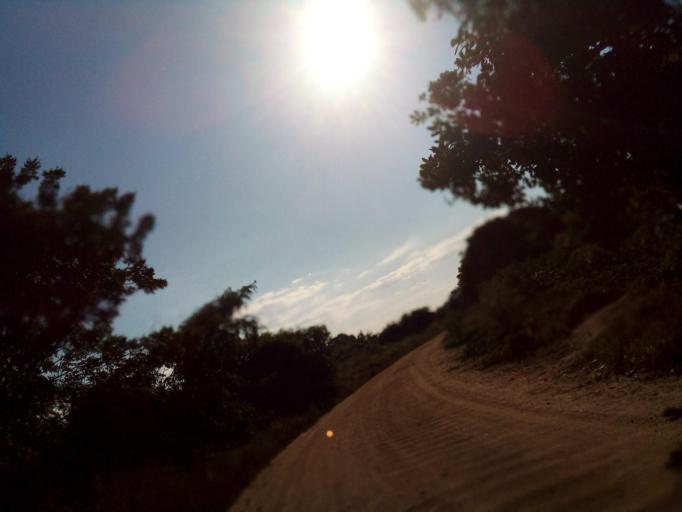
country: MZ
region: Zambezia
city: Quelimane
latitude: -17.4782
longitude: 36.5391
